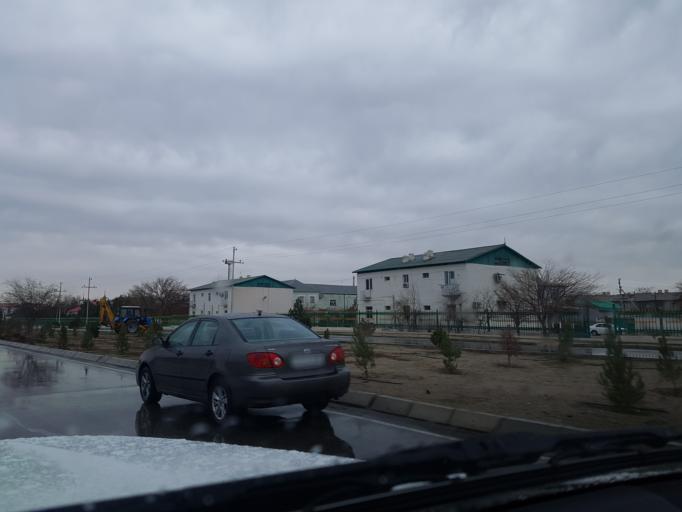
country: TM
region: Balkan
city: Balkanabat
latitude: 39.5094
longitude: 54.3473
